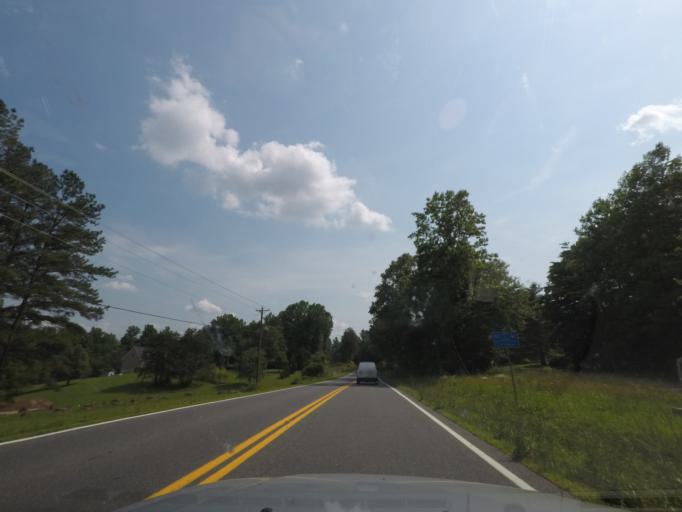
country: US
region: Virginia
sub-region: Fluvanna County
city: Palmyra
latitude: 37.8910
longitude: -78.2622
